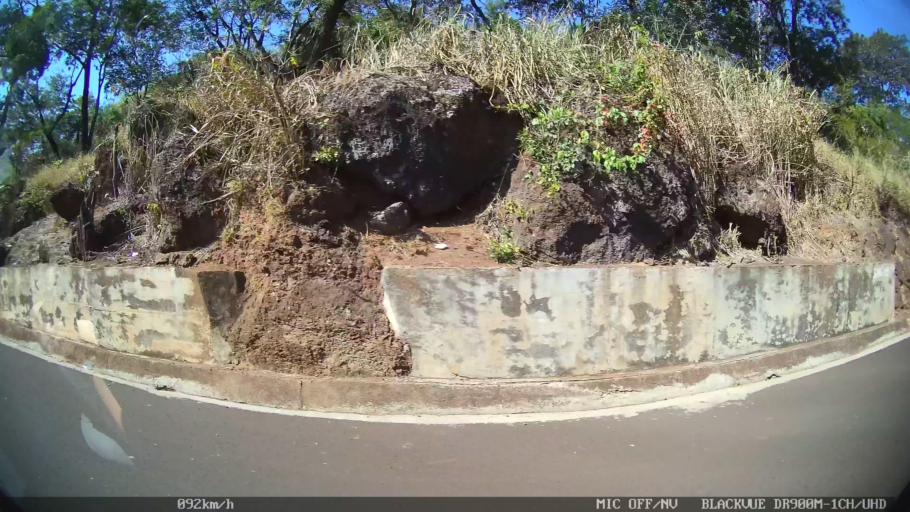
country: BR
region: Sao Paulo
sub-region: Batatais
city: Batatais
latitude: -20.7349
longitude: -47.5284
